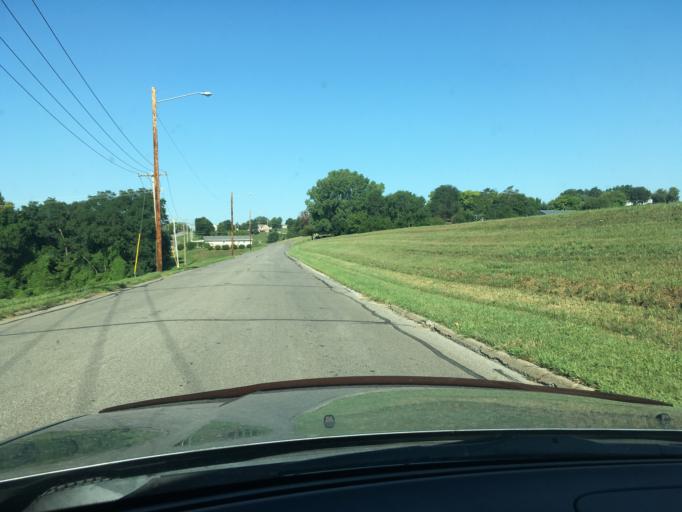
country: US
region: Kansas
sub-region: Atchison County
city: Atchison
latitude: 39.5784
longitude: -95.1176
